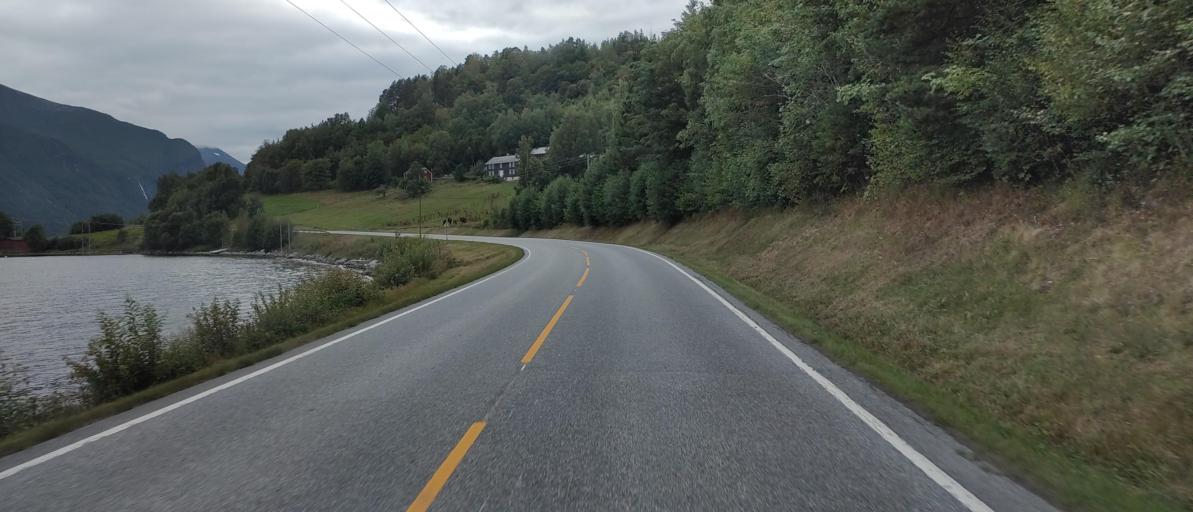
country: NO
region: More og Romsdal
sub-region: Rauma
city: Andalsnes
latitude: 62.5757
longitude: 7.6609
